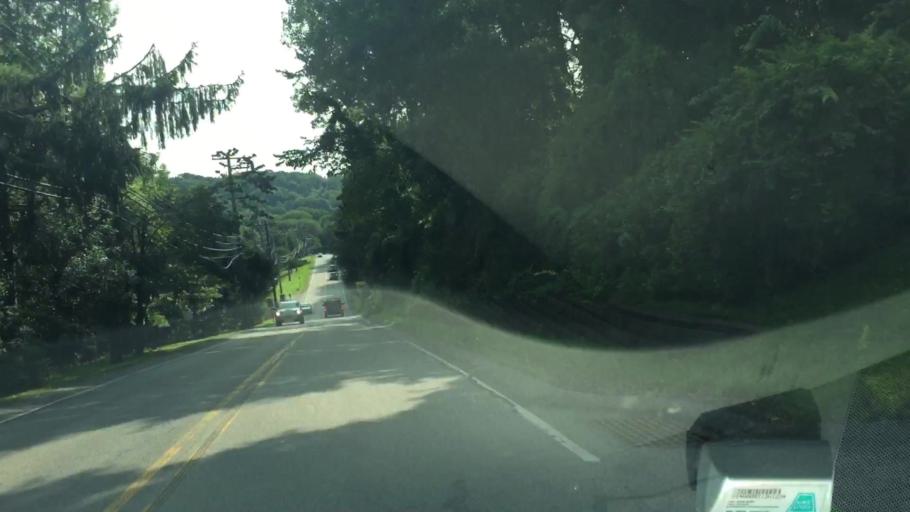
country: US
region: Pennsylvania
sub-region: Allegheny County
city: Fox Chapel
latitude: 40.5169
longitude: -79.8732
